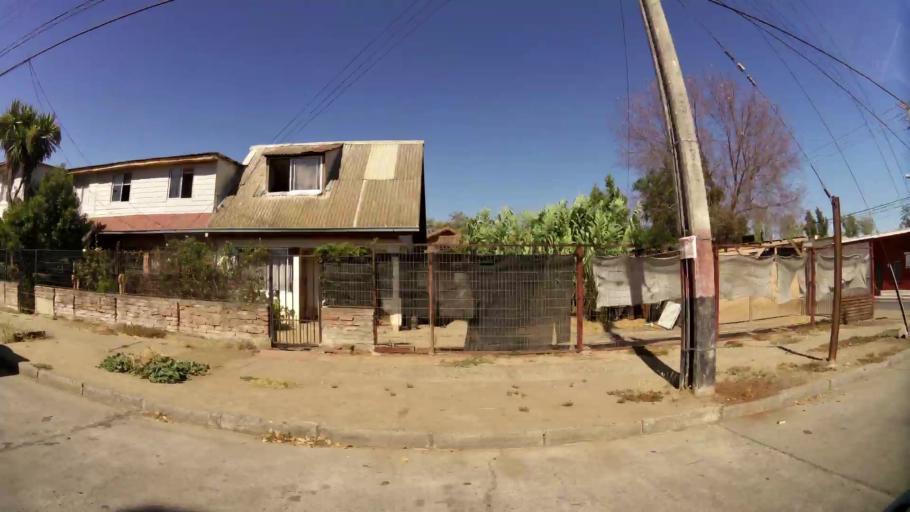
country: CL
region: Maule
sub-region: Provincia de Talca
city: Talca
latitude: -35.4338
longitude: -71.6647
